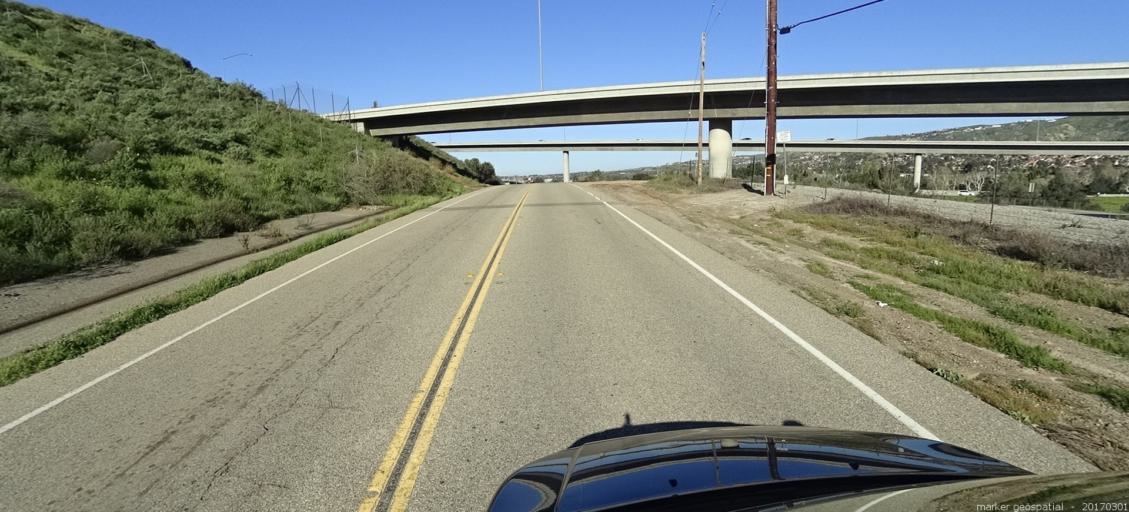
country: US
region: California
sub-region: Orange County
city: Yorba Linda
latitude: 33.8647
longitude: -117.7123
